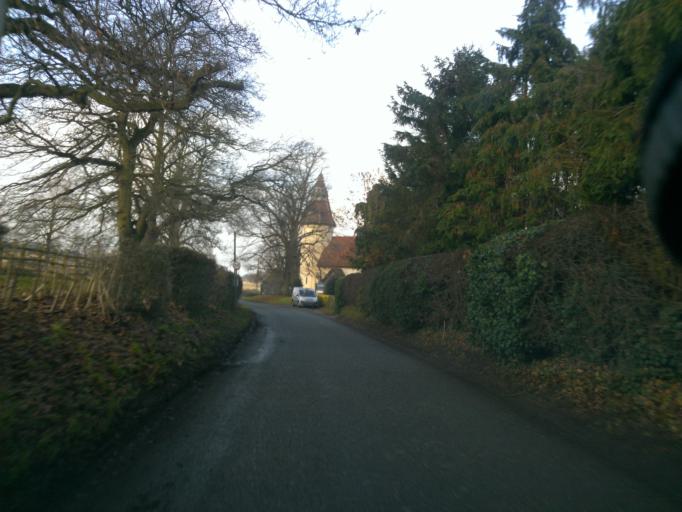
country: GB
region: England
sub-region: Suffolk
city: Sudbury
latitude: 51.9898
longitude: 0.7516
